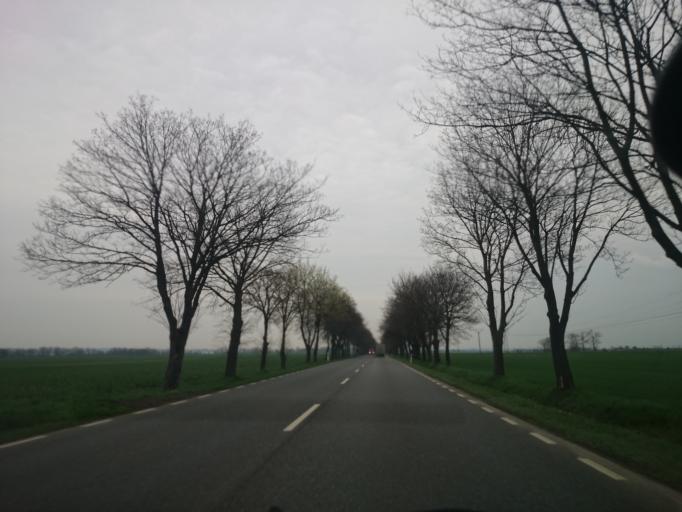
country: PL
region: Opole Voivodeship
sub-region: Powiat nyski
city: Paczkow
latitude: 50.4522
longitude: 17.0580
